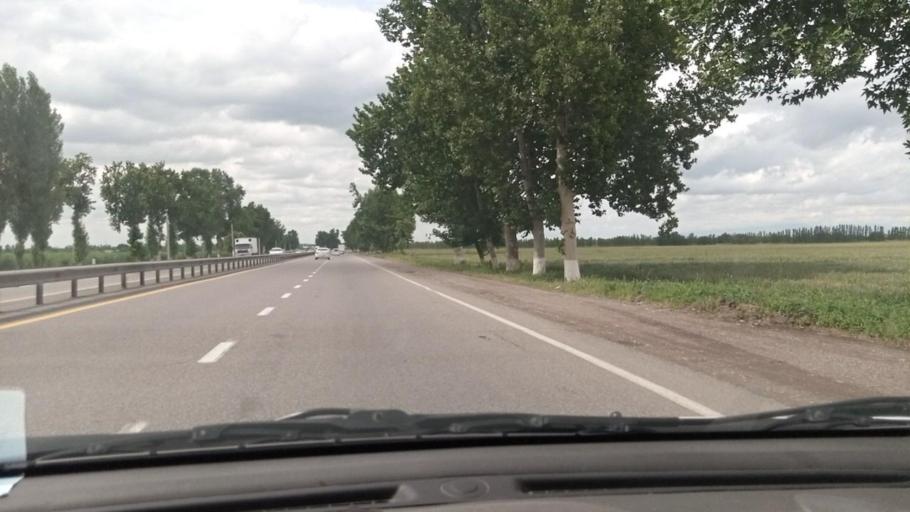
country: UZ
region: Toshkent Shahri
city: Bektemir
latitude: 41.1393
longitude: 69.4337
